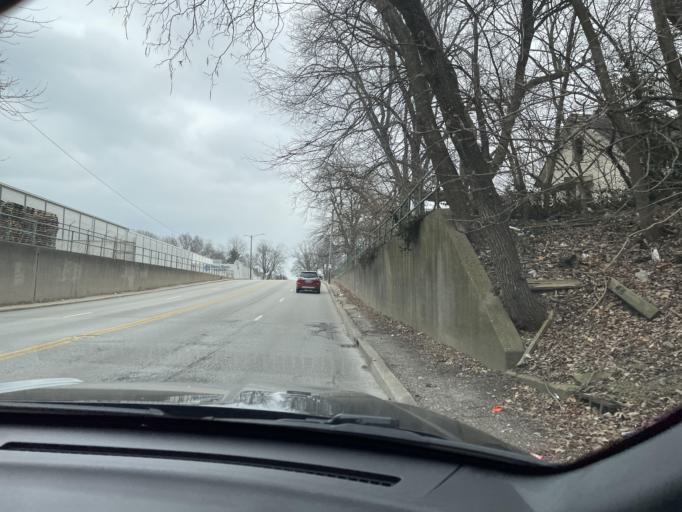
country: US
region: Illinois
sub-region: Sangamon County
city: Springfield
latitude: 39.7945
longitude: -89.6297
